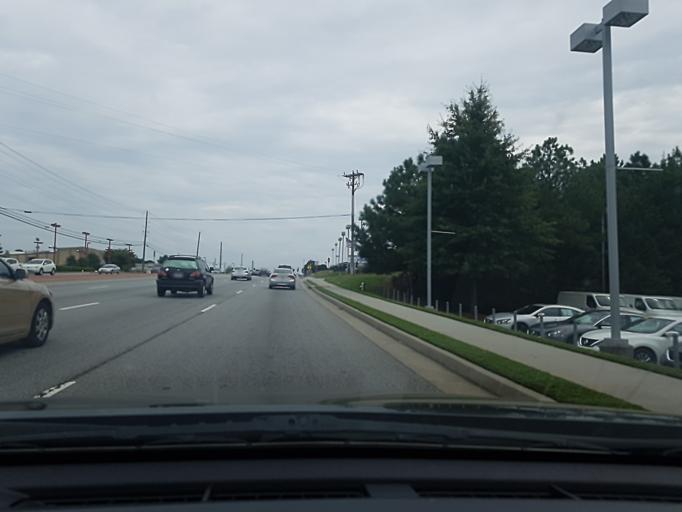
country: US
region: Georgia
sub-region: Gwinnett County
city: Duluth
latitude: 33.9680
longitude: -84.1445
